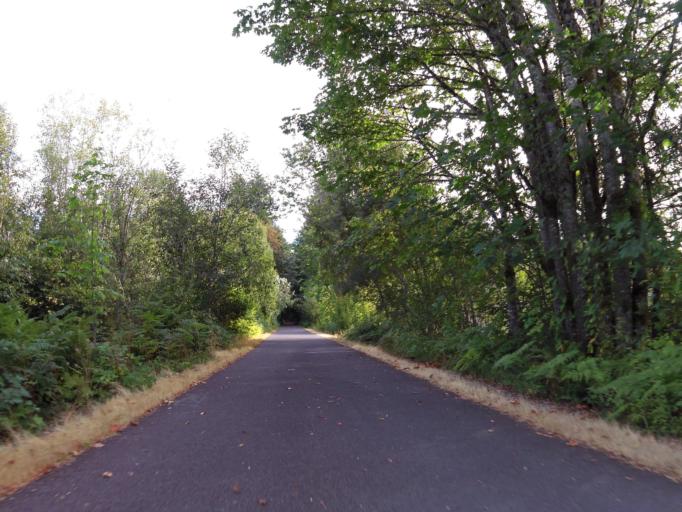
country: US
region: Washington
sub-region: Thurston County
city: Lacey
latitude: 46.9558
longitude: -122.8127
